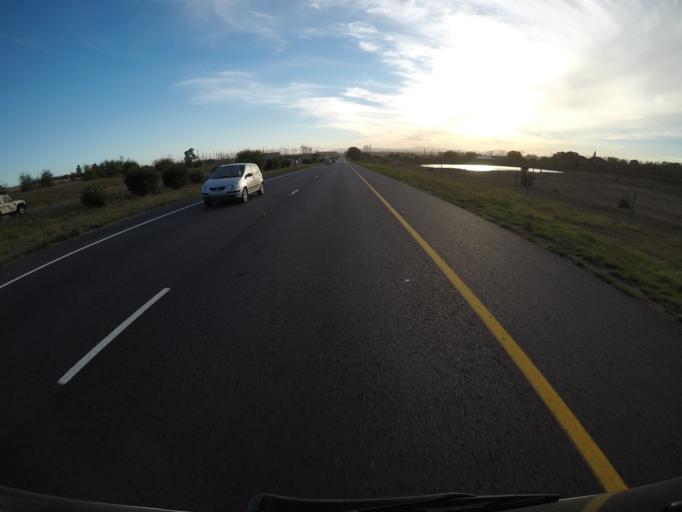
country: ZA
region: Western Cape
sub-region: City of Cape Town
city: Kraaifontein
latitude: -33.8136
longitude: 18.8135
